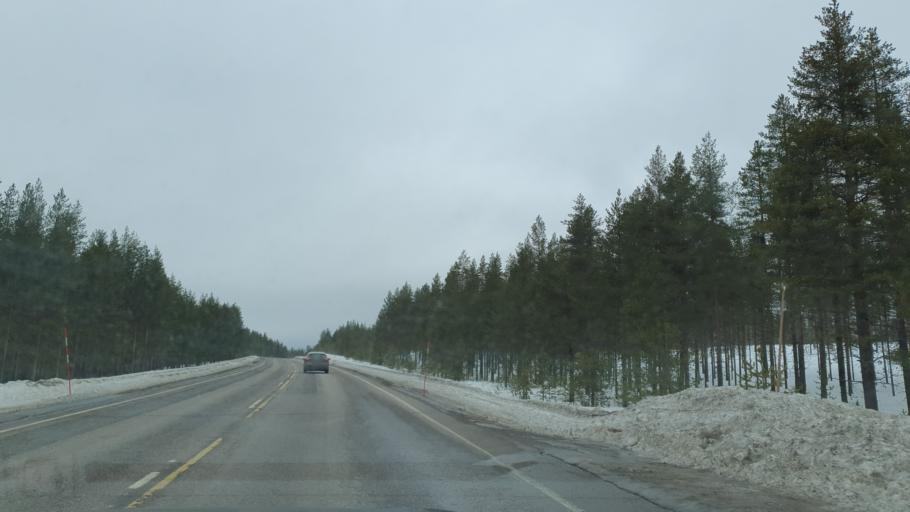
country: FI
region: Lapland
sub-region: Torniolaakso
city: Pello
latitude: 66.9192
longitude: 24.0918
